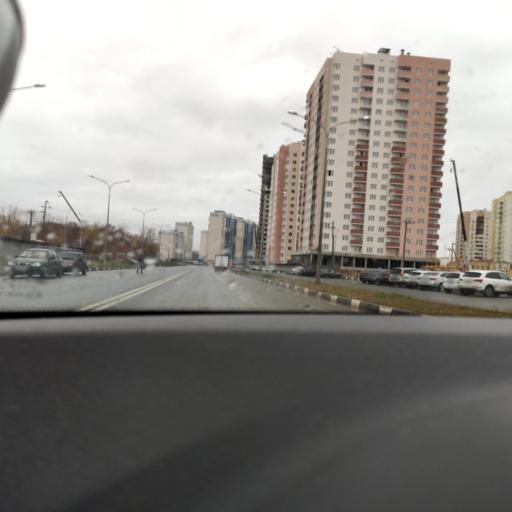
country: RU
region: Samara
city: Samara
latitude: 53.1452
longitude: 50.0762
